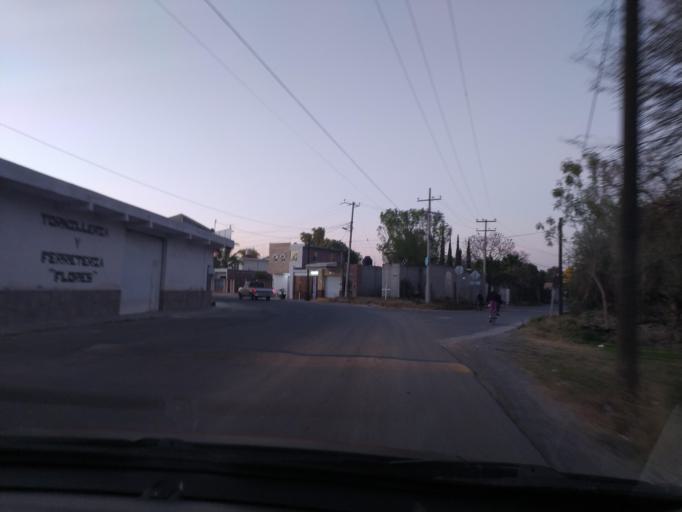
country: MX
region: Guanajuato
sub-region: San Francisco del Rincon
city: San Roque de Montes
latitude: 21.0150
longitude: -101.8149
